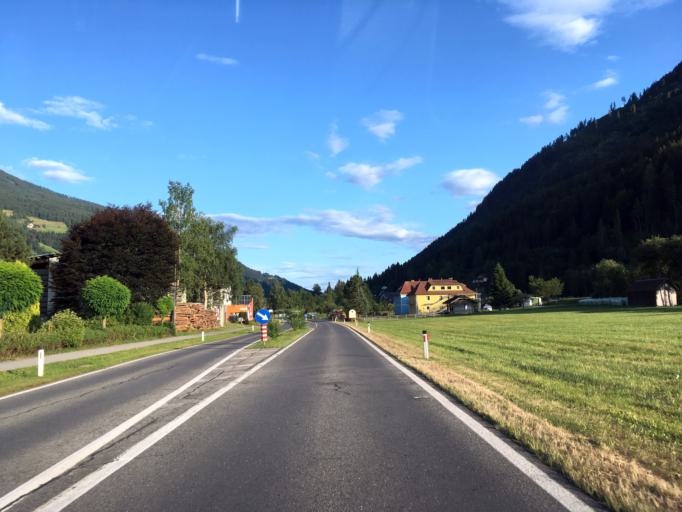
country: AT
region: Carinthia
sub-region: Politischer Bezirk Villach Land
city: Feld am See
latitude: 46.7828
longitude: 13.7386
